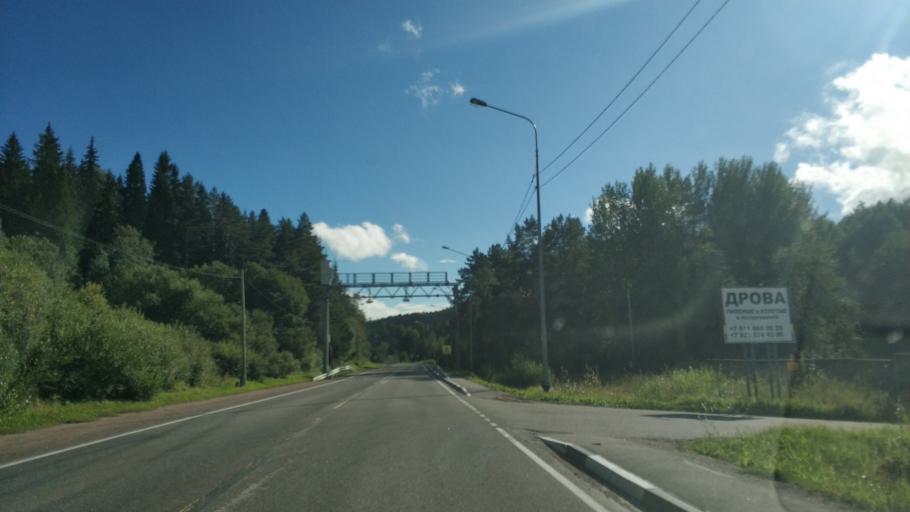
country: RU
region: Republic of Karelia
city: Sortavala
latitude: 61.6743
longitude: 30.6547
